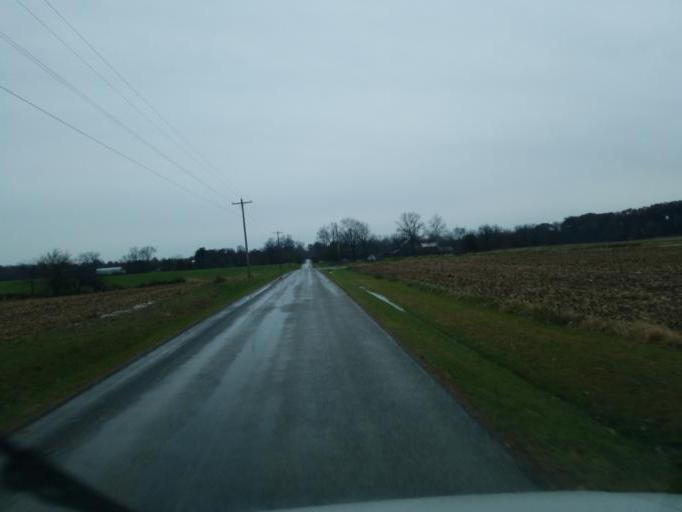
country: US
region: Ohio
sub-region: Delaware County
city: Ashley
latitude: 40.3896
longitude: -82.9363
